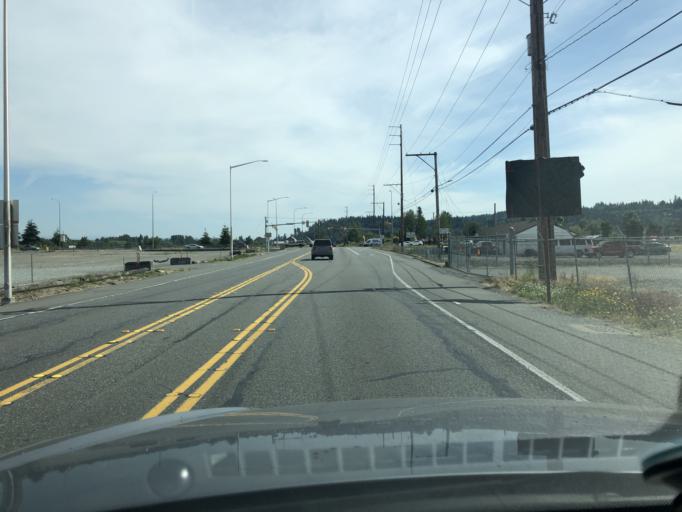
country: US
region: Washington
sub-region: King County
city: Kent
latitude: 47.3551
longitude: -122.2495
